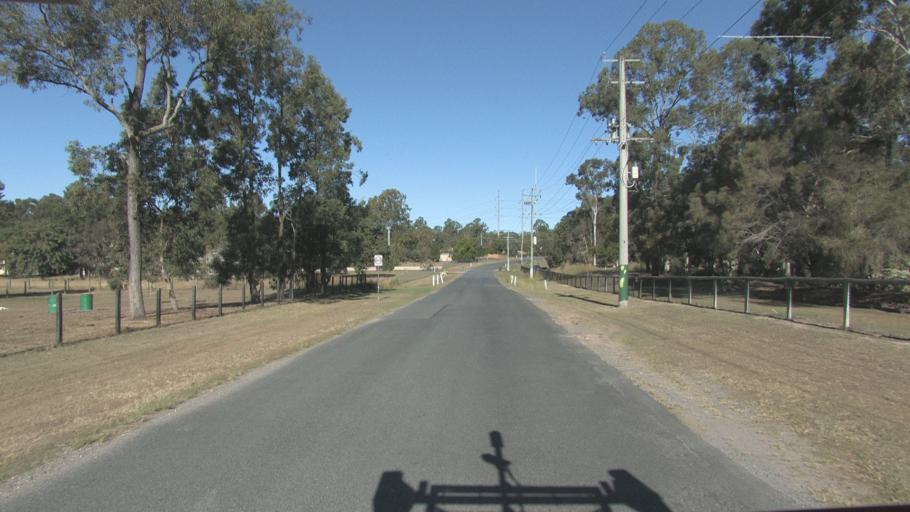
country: AU
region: Queensland
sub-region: Logan
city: Park Ridge South
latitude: -27.7305
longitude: 153.0208
